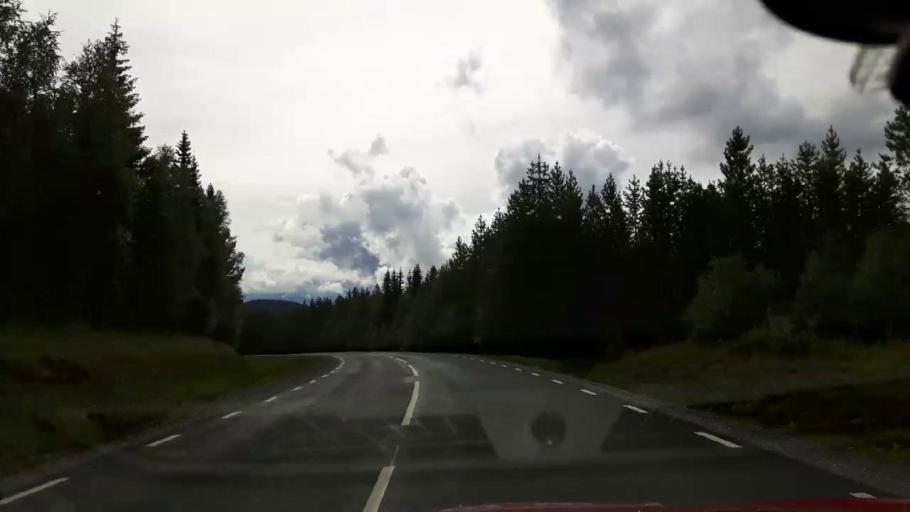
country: NO
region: Nord-Trondelag
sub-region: Lierne
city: Sandvika
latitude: 64.6387
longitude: 14.1364
